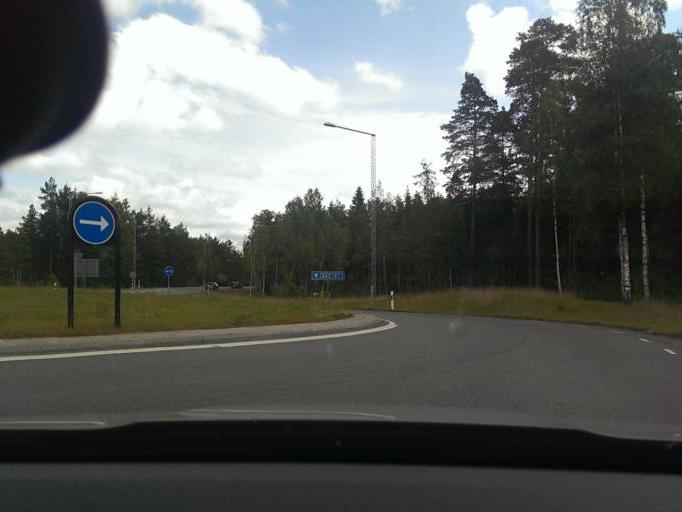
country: SE
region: Joenkoeping
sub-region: Varnamo Kommun
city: Varnamo
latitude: 57.1929
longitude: 14.0642
